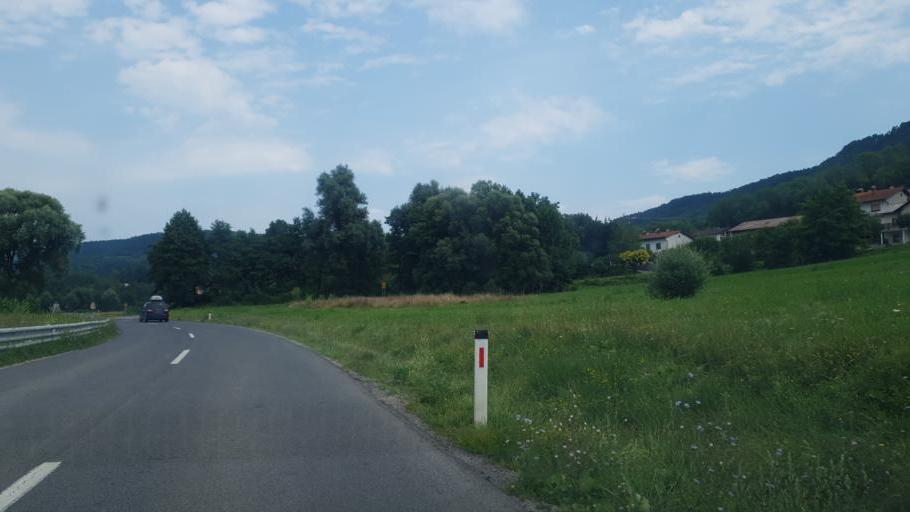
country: SI
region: Ilirska Bistrica
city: Ilirska Bistrica
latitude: 45.5777
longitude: 14.2374
